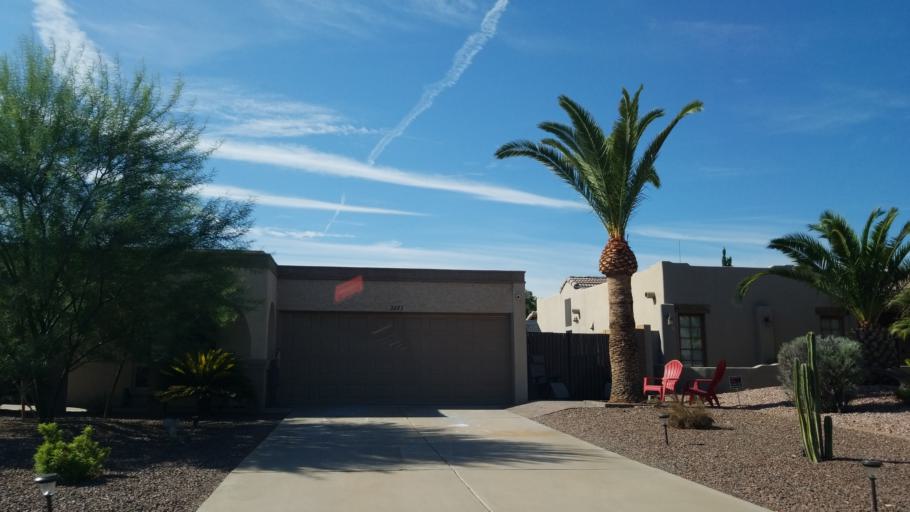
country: US
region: Arizona
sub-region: Maricopa County
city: Paradise Valley
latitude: 33.5870
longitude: -112.0121
